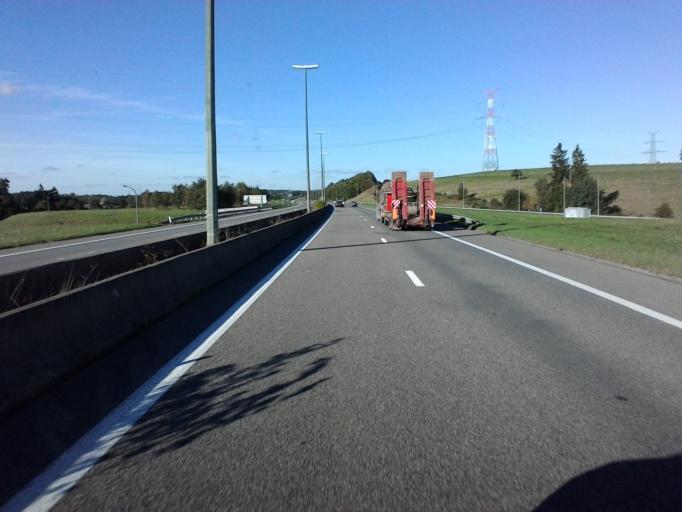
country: BE
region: Wallonia
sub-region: Province du Luxembourg
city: Bastogne
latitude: 50.0183
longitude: 5.6956
